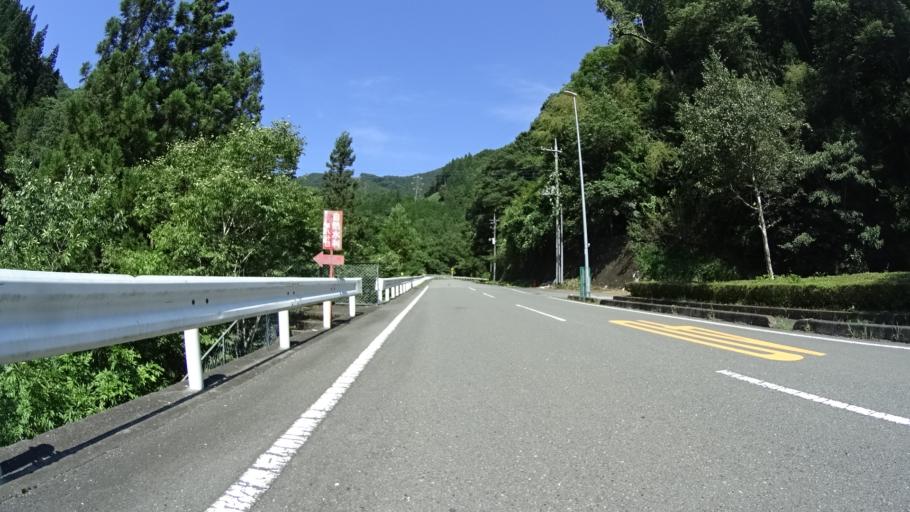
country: JP
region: Gunma
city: Tomioka
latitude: 36.0567
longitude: 138.8581
